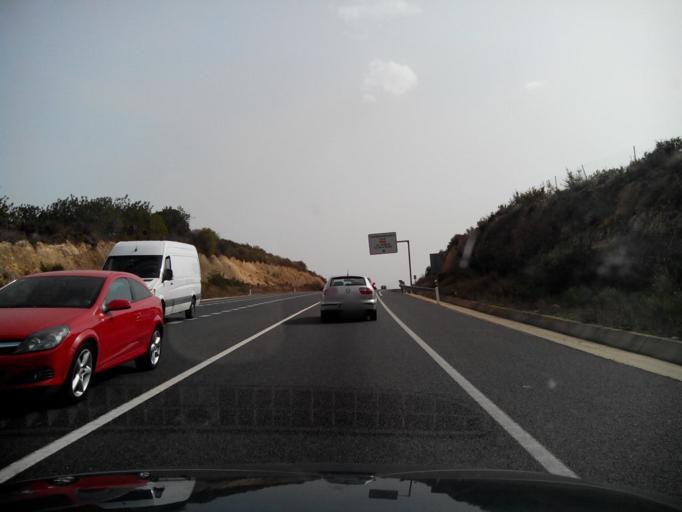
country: ES
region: Catalonia
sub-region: Provincia de Tarragona
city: Torredembarra
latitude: 41.1621
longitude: 1.4100
